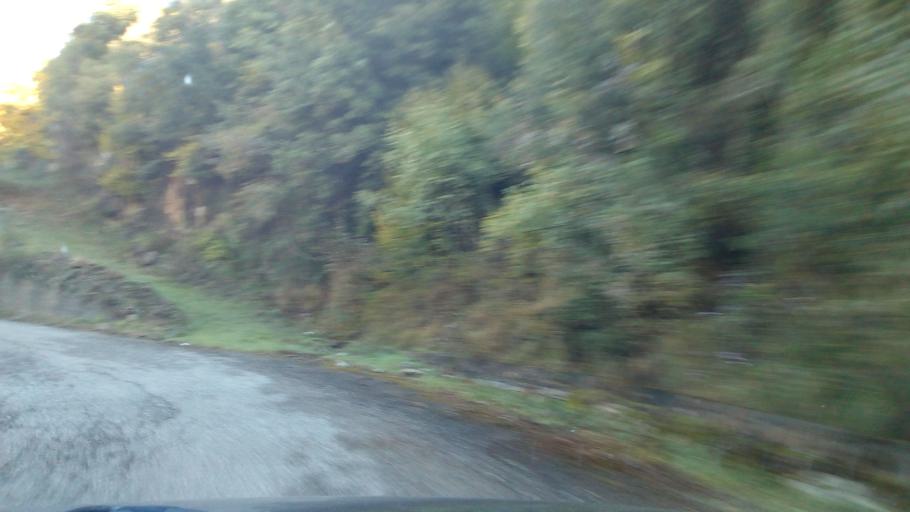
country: GR
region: West Greece
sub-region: Nomos Aitolias kai Akarnanias
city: Nafpaktos
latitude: 38.5610
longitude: 21.8527
